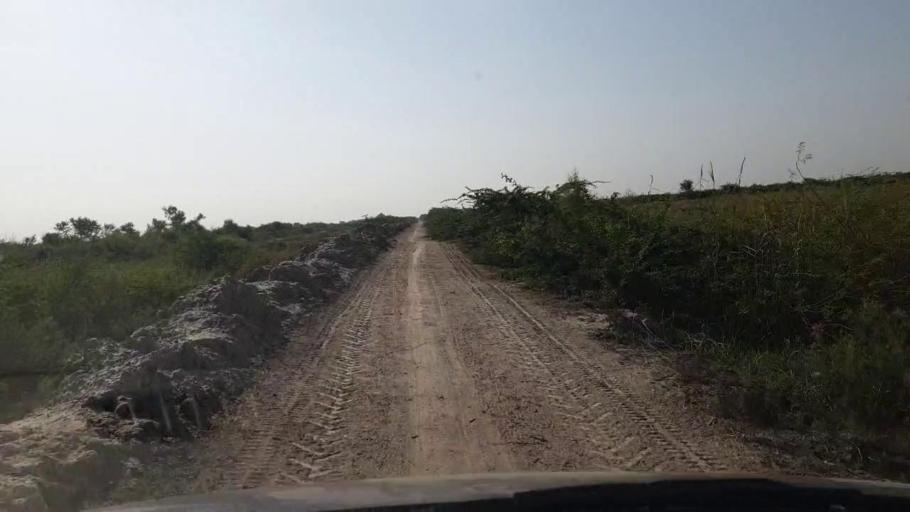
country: PK
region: Sindh
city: Kadhan
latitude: 24.6066
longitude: 69.0737
